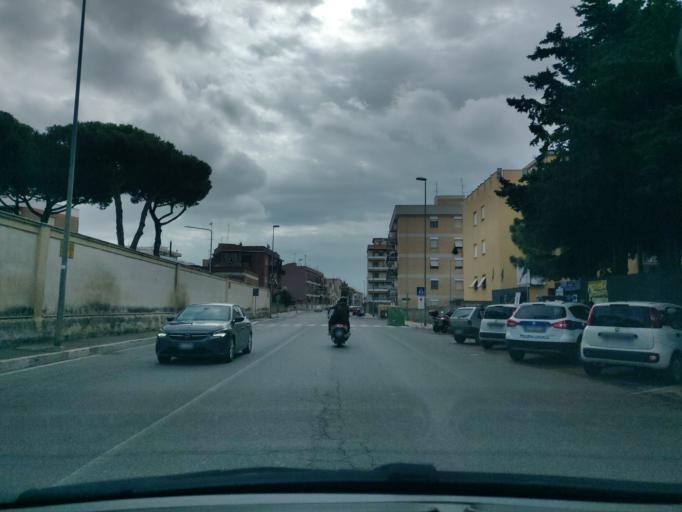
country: IT
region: Latium
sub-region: Citta metropolitana di Roma Capitale
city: Civitavecchia
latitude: 42.0972
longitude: 11.8018
